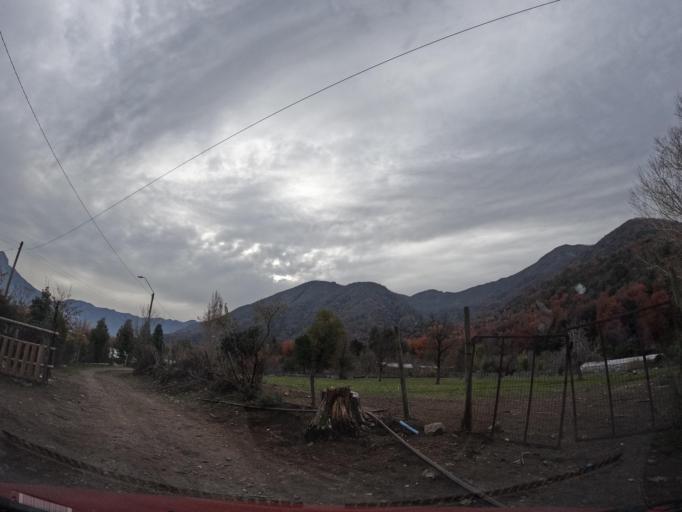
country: CL
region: Maule
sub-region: Provincia de Linares
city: Colbun
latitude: -35.7229
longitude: -71.0178
